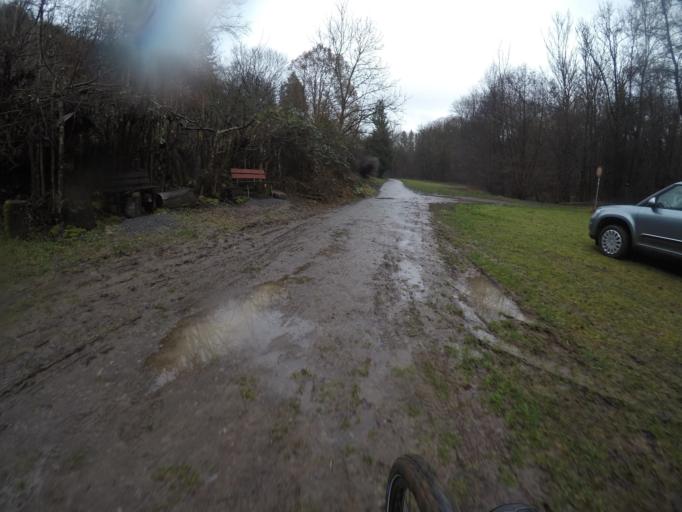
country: DE
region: Baden-Wuerttemberg
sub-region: Regierungsbezirk Stuttgart
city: Bietigheim-Bissingen
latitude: 48.9613
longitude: 9.0896
